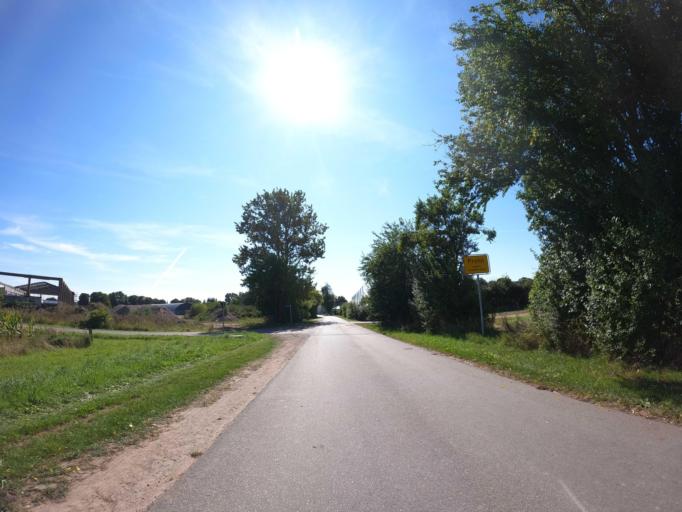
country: DE
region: Mecklenburg-Vorpommern
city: Prohn
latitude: 54.3793
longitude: 13.0226
